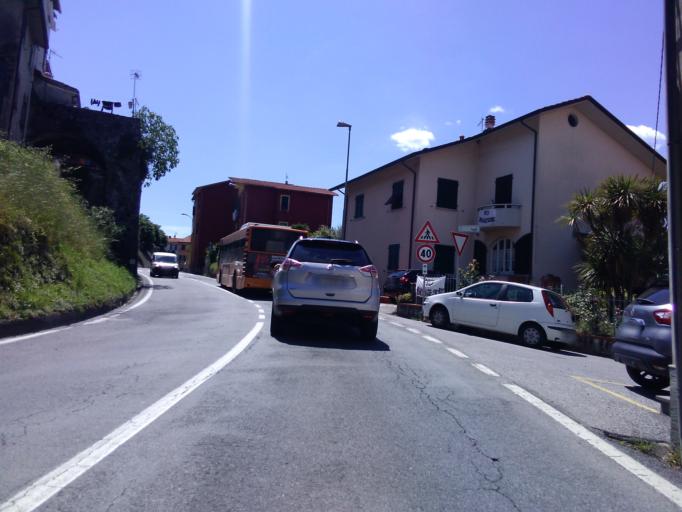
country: IT
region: Tuscany
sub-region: Provincia di Massa-Carrara
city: Albiano Magra
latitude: 44.1659
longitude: 9.9173
